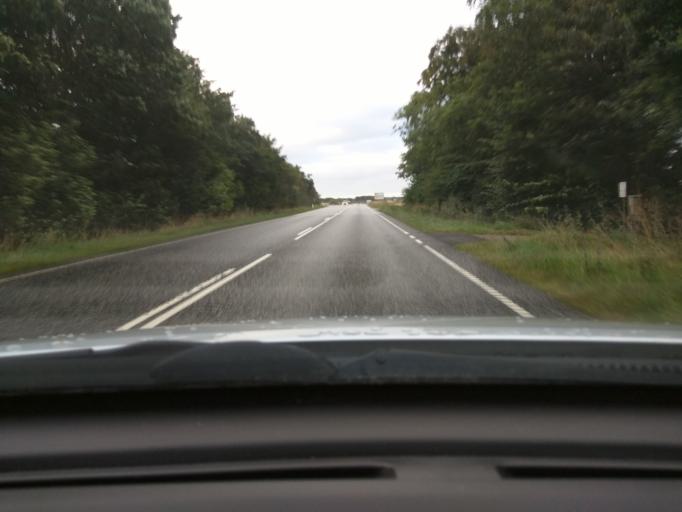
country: DK
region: Central Jutland
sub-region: Silkeborg Kommune
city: Kjellerup
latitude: 56.3059
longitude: 9.3250
